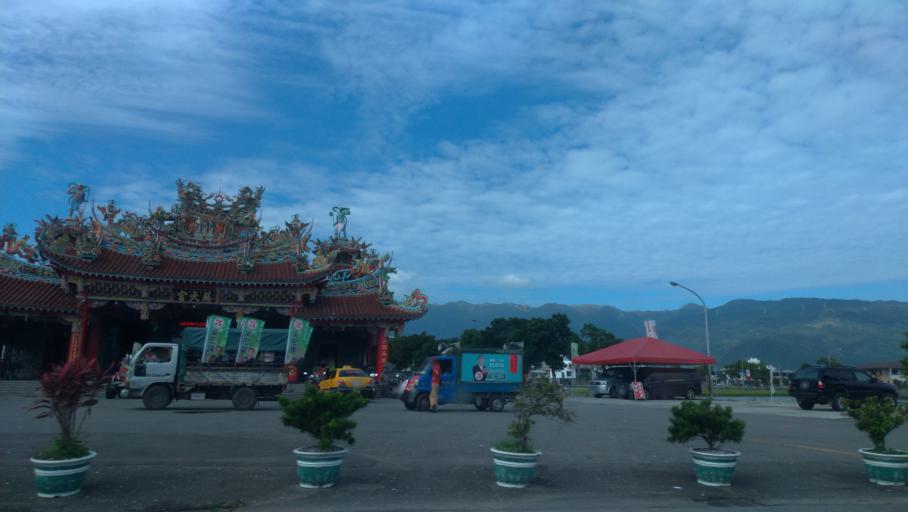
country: TW
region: Taiwan
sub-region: Yilan
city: Yilan
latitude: 24.7978
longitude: 121.7866
